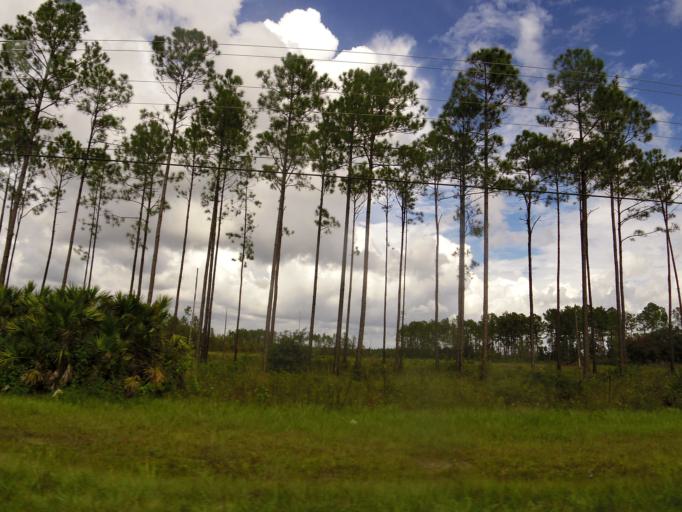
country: US
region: Florida
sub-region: Duval County
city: Baldwin
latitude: 30.1481
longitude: -82.0177
